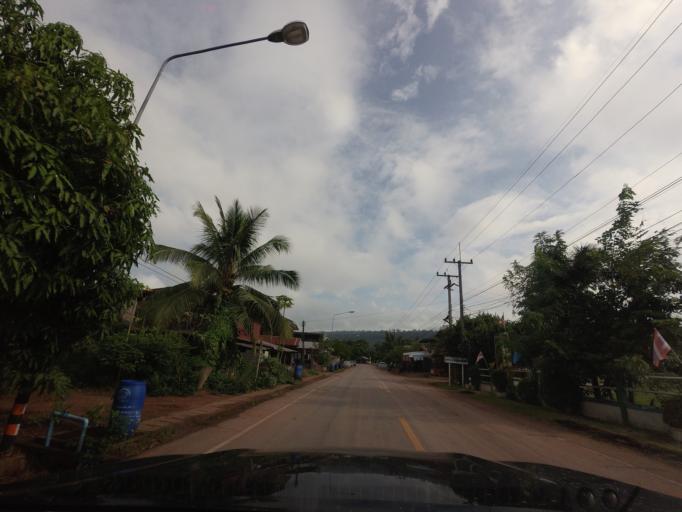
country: TH
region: Changwat Udon Thani
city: Nam Som
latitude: 17.8609
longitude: 102.2563
